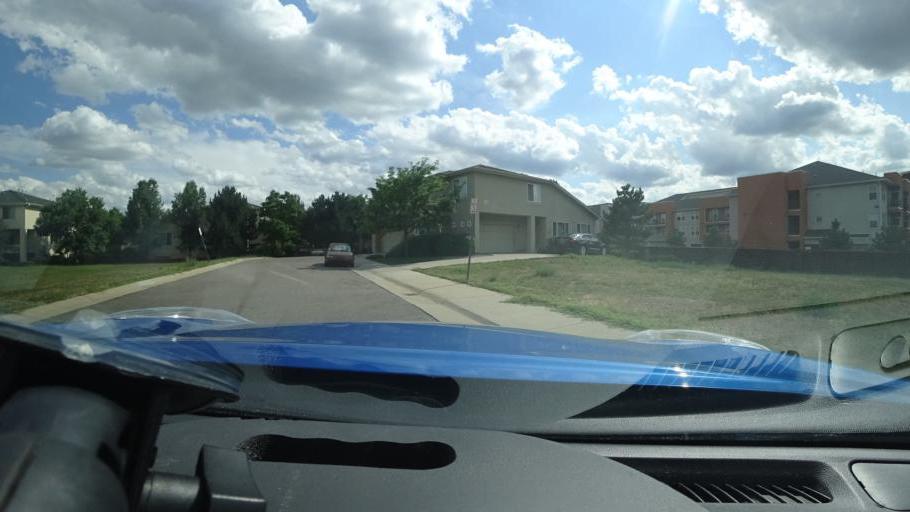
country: US
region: Colorado
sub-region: Adams County
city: Aurora
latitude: 39.6943
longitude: -104.8595
